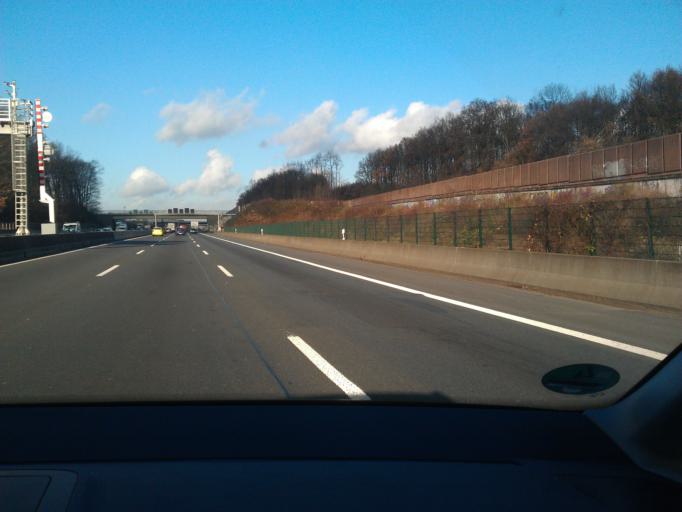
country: DE
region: North Rhine-Westphalia
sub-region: Regierungsbezirk Koln
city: Mengenich
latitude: 50.9453
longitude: 6.8497
